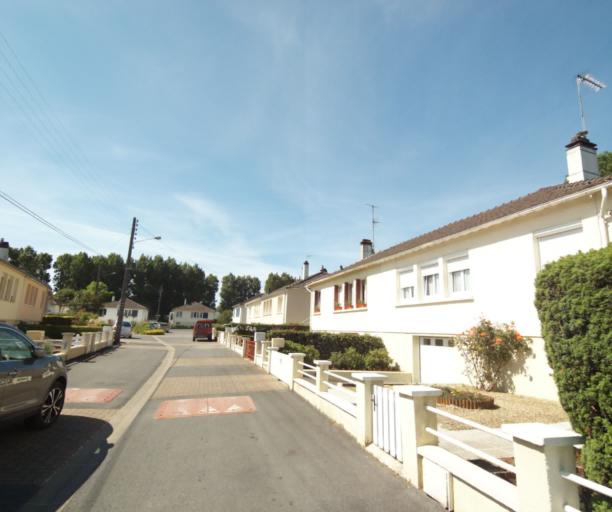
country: FR
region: Champagne-Ardenne
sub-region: Departement des Ardennes
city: Charleville-Mezieres
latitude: 49.7516
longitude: 4.7143
